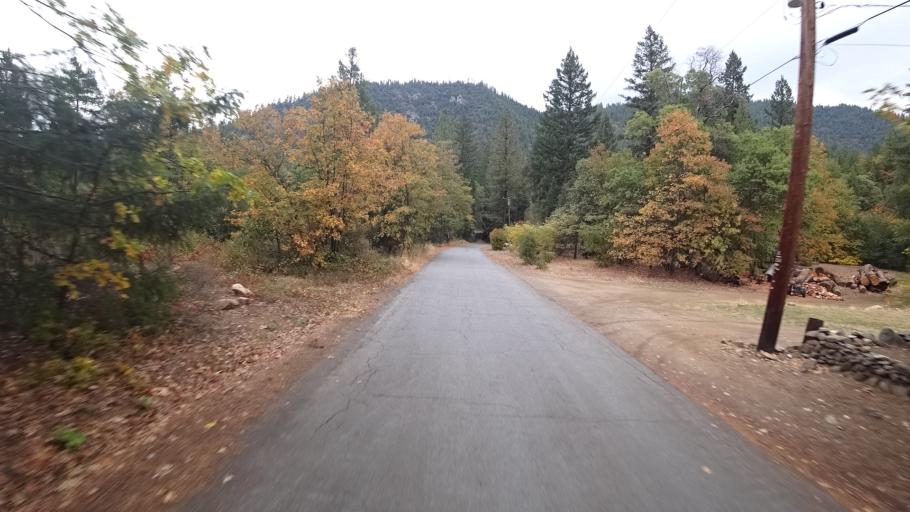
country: US
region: California
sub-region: Siskiyou County
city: Happy Camp
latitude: 41.8329
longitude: -123.1732
